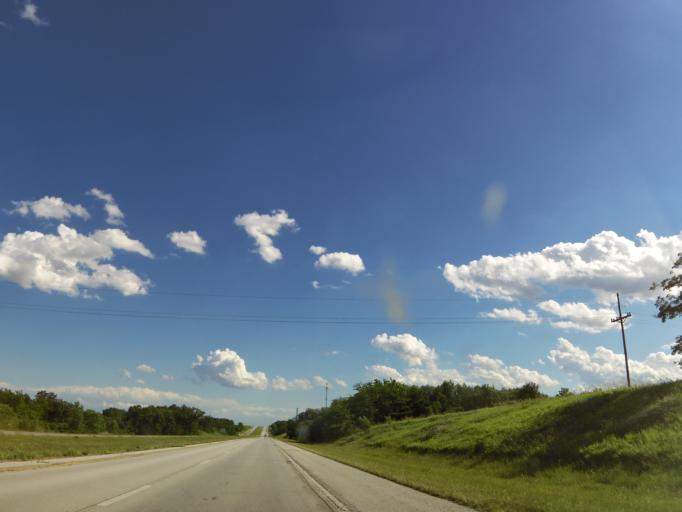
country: US
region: Missouri
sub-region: Lewis County
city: Canton
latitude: 40.0342
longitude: -91.5258
